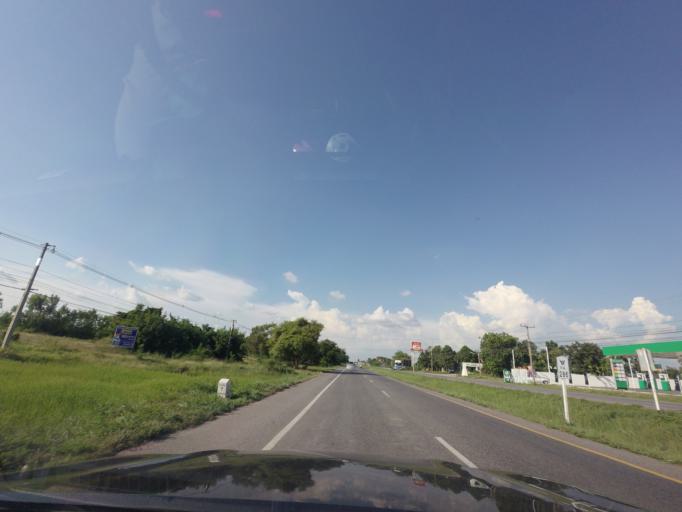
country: TH
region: Khon Kaen
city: Non Sila
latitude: 15.9940
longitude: 102.6998
